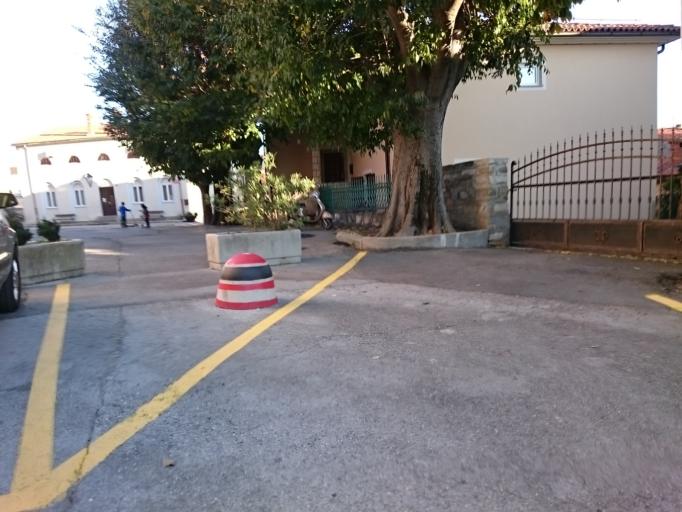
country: SI
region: Izola-Isola
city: Izola
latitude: 45.5399
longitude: 13.6583
